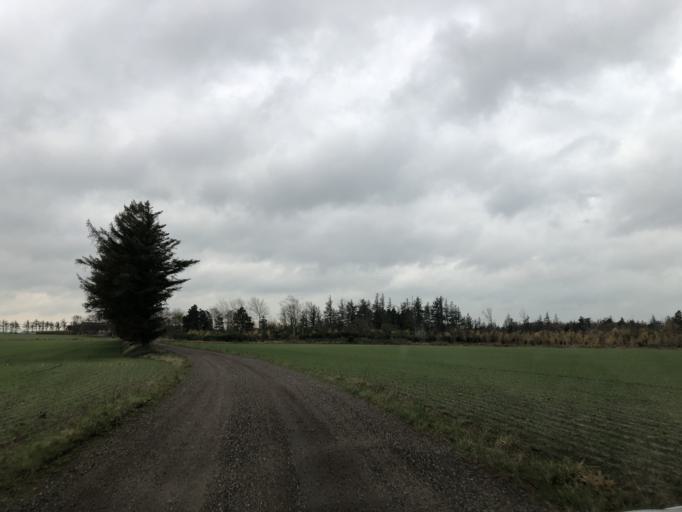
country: DK
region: Central Jutland
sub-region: Holstebro Kommune
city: Ulfborg
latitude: 56.3064
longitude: 8.2003
